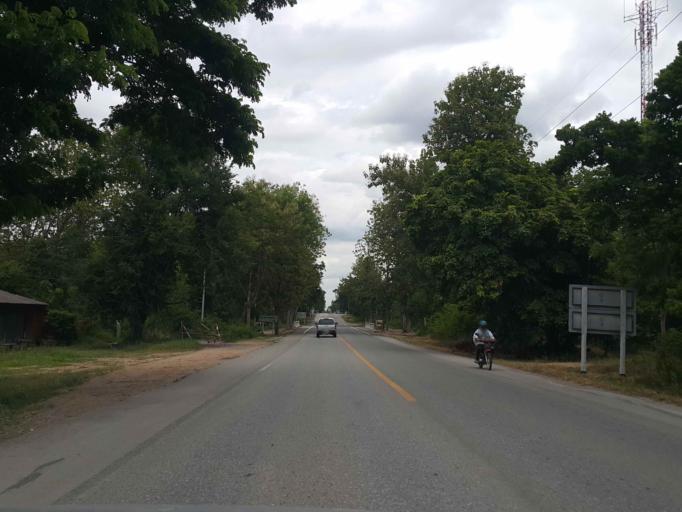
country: TH
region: Chiang Mai
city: Doi Lo
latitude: 18.4236
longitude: 98.8599
